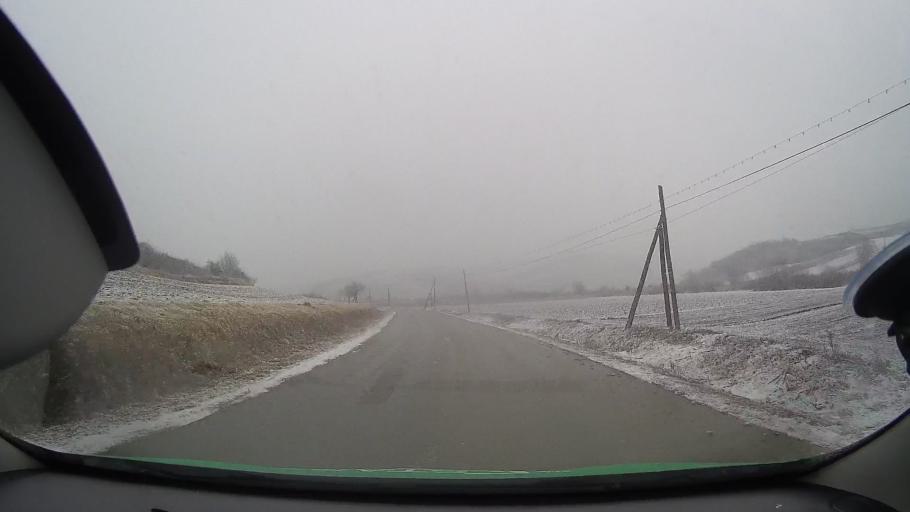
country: RO
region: Alba
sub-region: Comuna Lopadea Noua
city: Lopadea Noua
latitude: 46.2918
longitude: 23.8364
